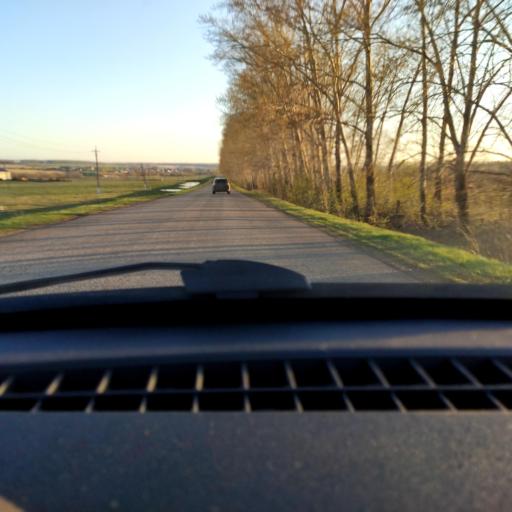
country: RU
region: Bashkortostan
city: Avdon
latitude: 54.4979
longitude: 55.6160
